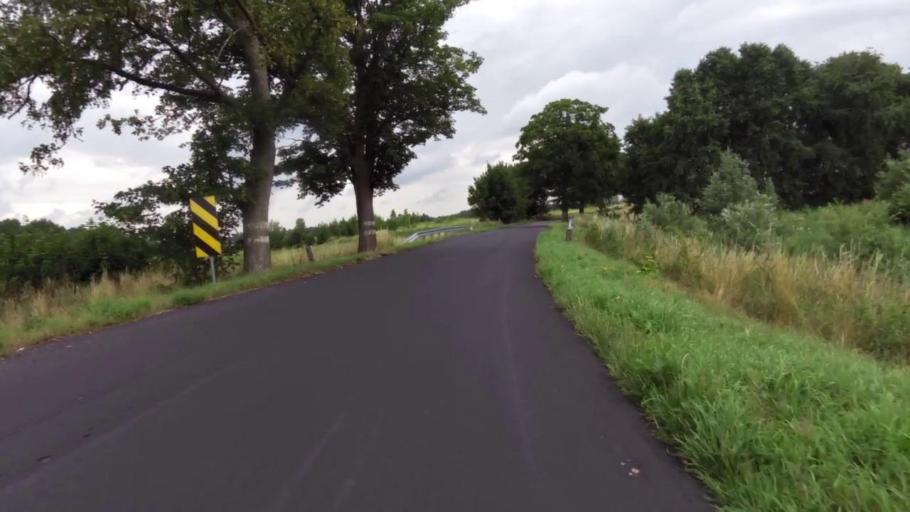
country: PL
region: West Pomeranian Voivodeship
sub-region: Powiat mysliborski
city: Mysliborz
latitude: 52.9619
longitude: 14.8846
